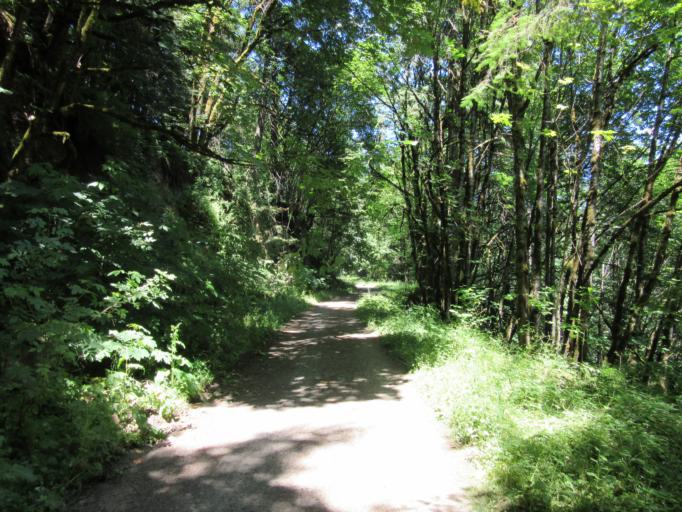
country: US
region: Oregon
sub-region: Washington County
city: West Haven
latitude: 45.5555
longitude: -122.7528
